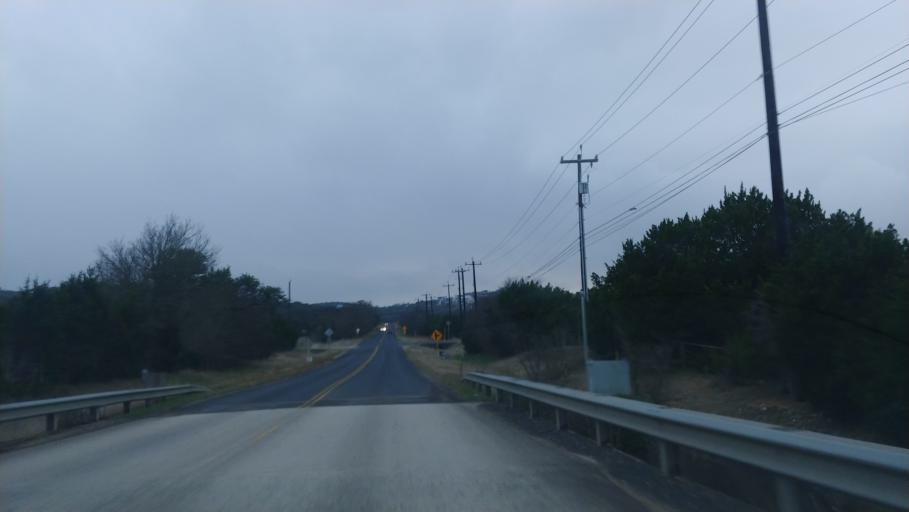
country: US
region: Texas
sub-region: Bexar County
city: Cross Mountain
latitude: 29.6739
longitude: -98.6754
